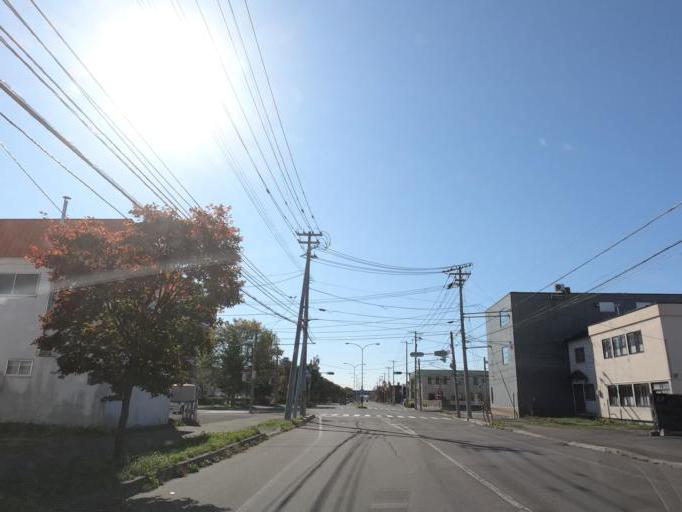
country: JP
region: Hokkaido
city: Obihiro
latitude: 42.9181
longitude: 143.2122
